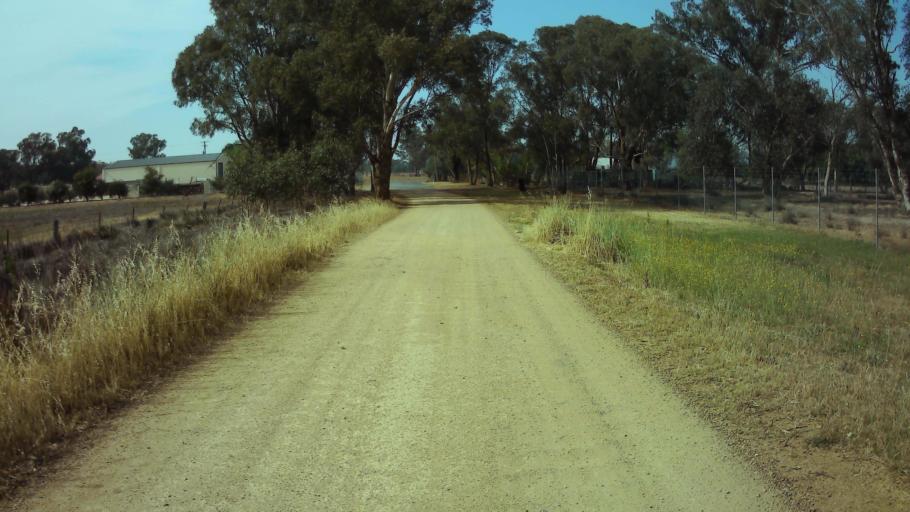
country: AU
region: New South Wales
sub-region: Weddin
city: Grenfell
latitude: -33.9039
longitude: 148.1470
